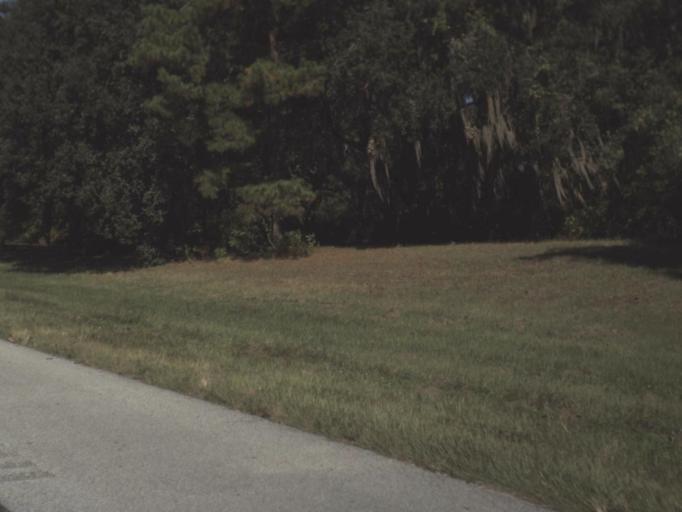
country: US
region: Florida
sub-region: Sumter County
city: Wildwood
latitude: 28.8162
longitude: -82.0165
